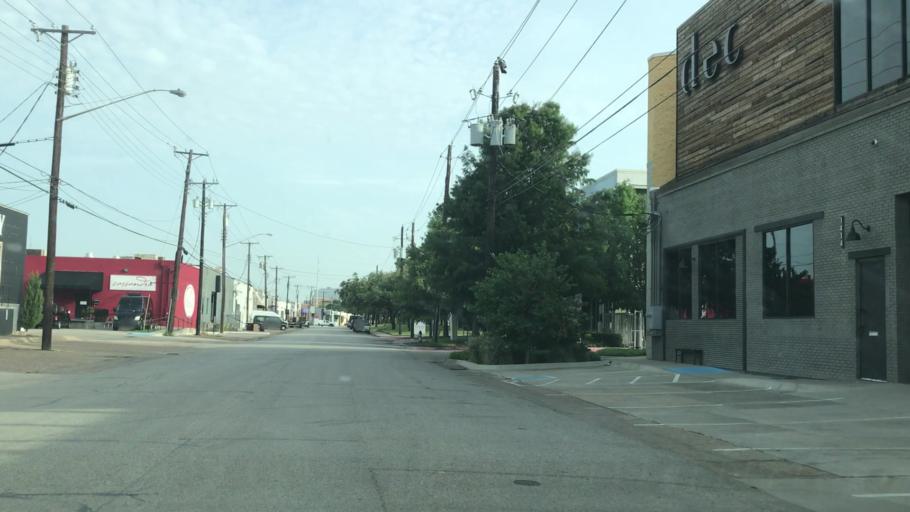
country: US
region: Texas
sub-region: Dallas County
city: Dallas
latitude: 32.7908
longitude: -96.8193
